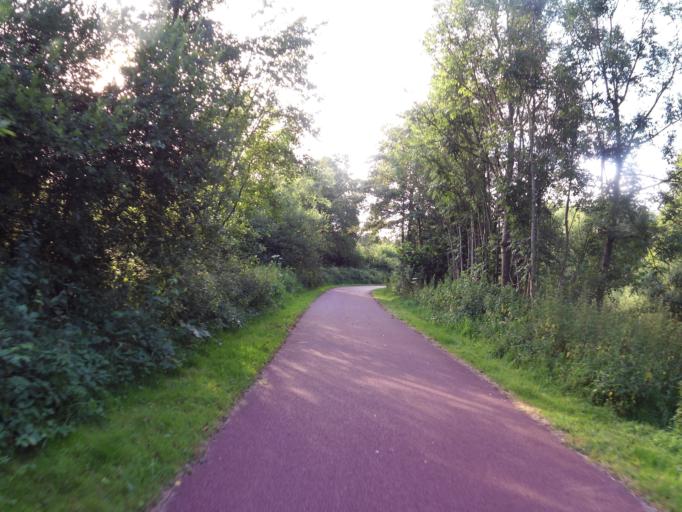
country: NL
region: North Brabant
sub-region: Gemeente Geldrop-Mierlo
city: Geldrop
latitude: 51.4314
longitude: 5.5506
